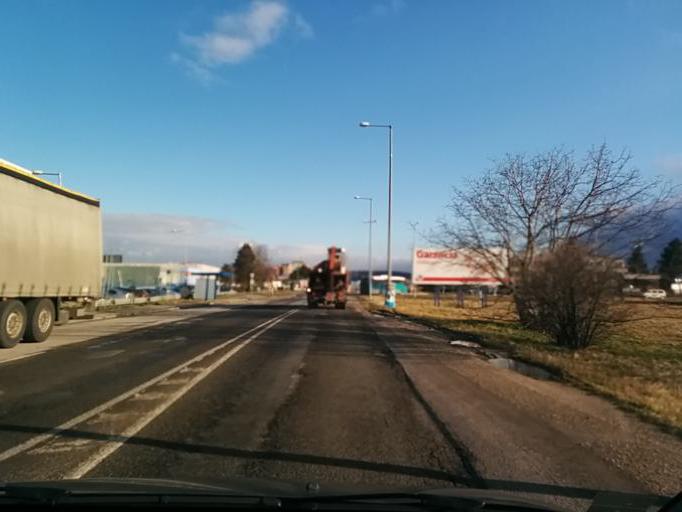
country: SK
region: Trenciansky
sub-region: Okres Nove Mesto nad Vahom
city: Nove Mesto nad Vahom
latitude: 48.7424
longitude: 17.8371
